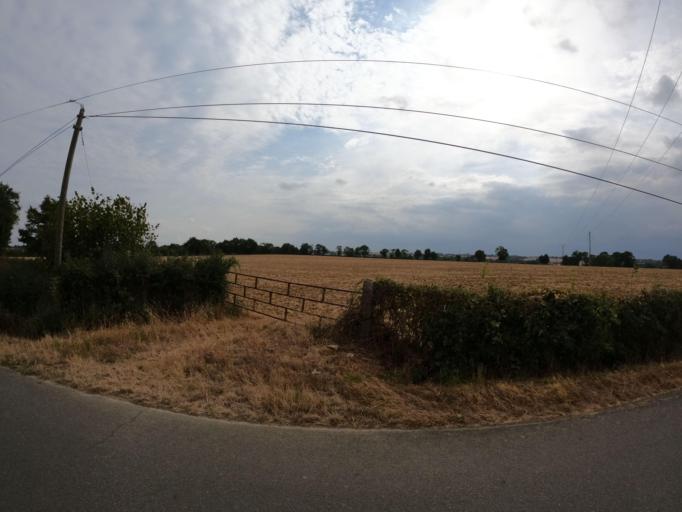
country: FR
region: Pays de la Loire
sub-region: Departement de Maine-et-Loire
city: Saint-Christophe-du-Bois
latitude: 47.0306
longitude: -0.9563
